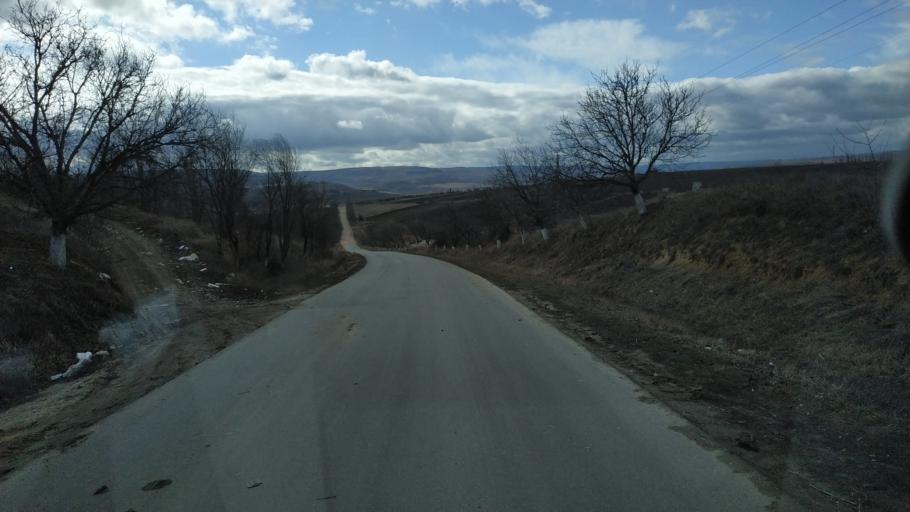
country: MD
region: Stinga Nistrului
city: Bucovat
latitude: 47.2009
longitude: 28.4917
